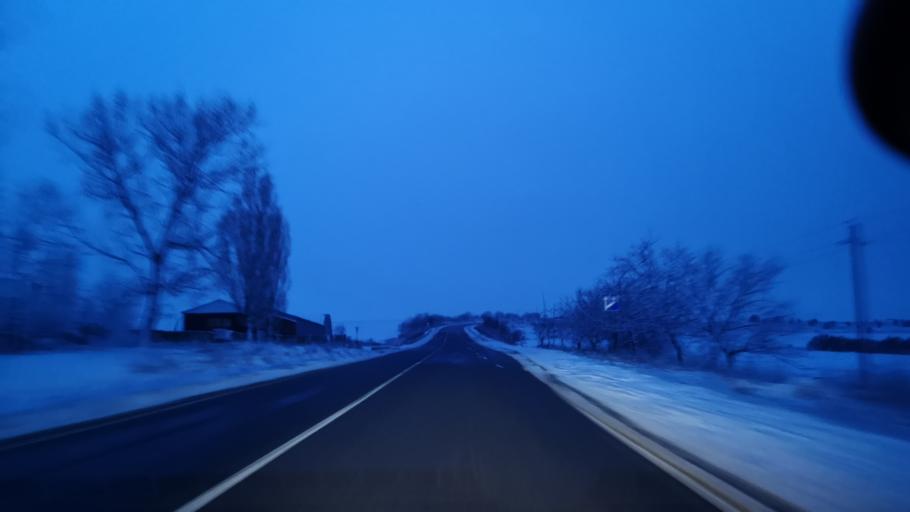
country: MD
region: Rezina
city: Saharna
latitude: 47.5902
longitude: 28.8212
